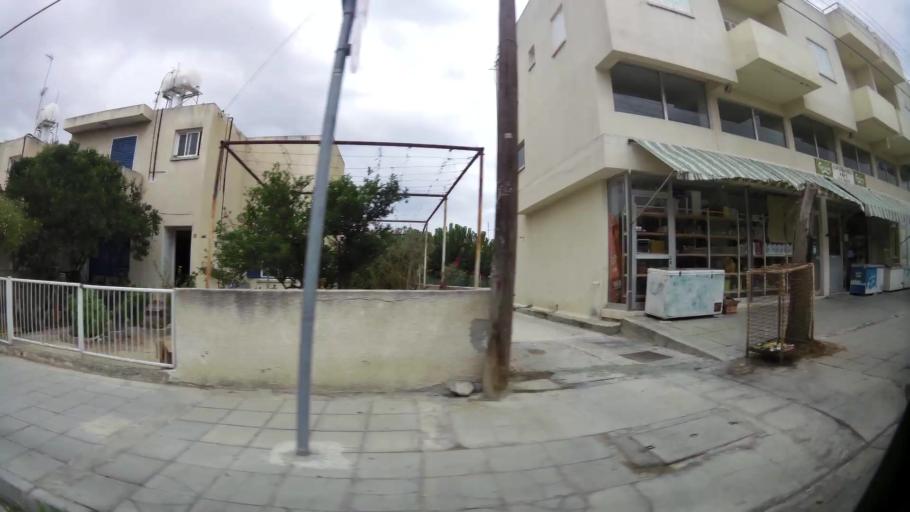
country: CY
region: Lefkosia
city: Geri
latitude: 35.1118
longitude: 33.3882
